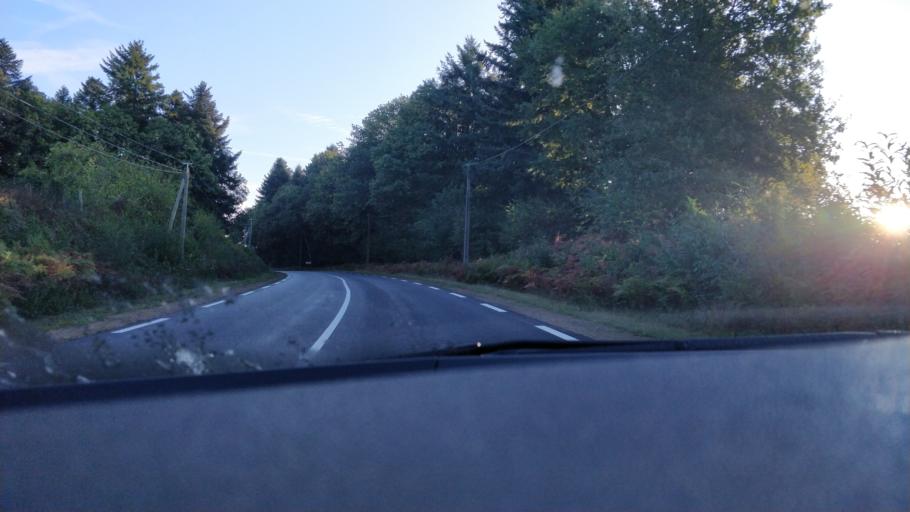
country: FR
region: Limousin
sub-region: Departement de la Haute-Vienne
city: Sauviat-sur-Vige
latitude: 45.8770
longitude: 1.5477
